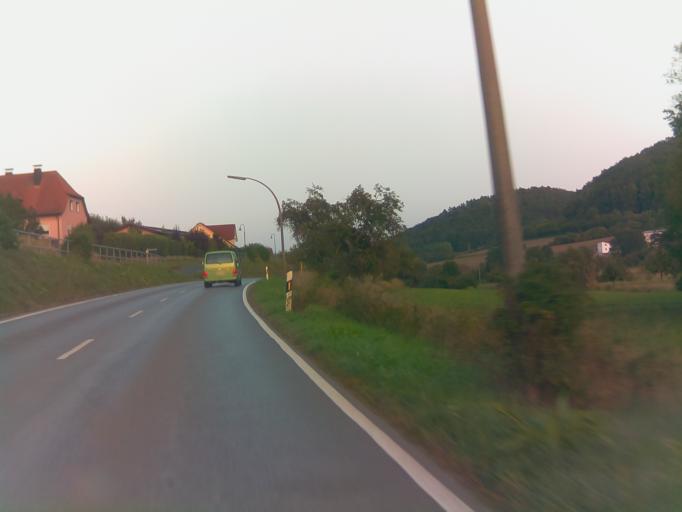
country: DE
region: Bavaria
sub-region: Regierungsbezirk Unterfranken
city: Euerdorf
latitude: 50.1429
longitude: 10.0291
